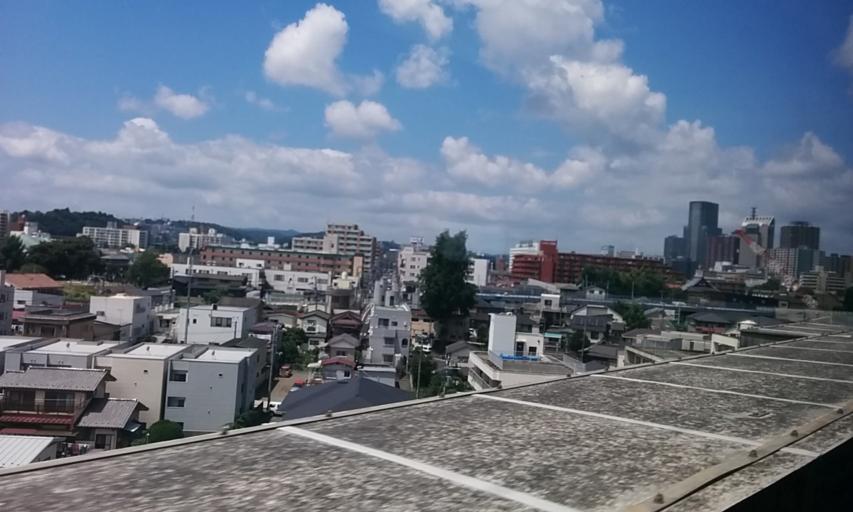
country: JP
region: Miyagi
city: Sendai
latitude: 38.2475
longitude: 140.8916
